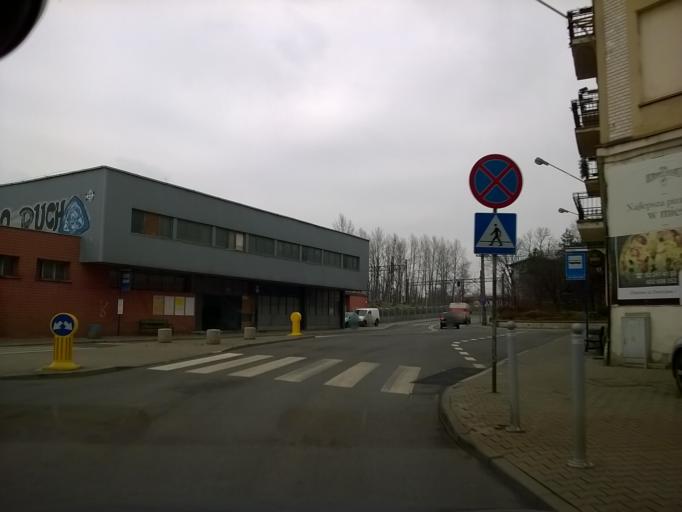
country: PL
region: Silesian Voivodeship
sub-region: Chorzow
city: Chorzow
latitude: 50.2983
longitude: 18.9502
